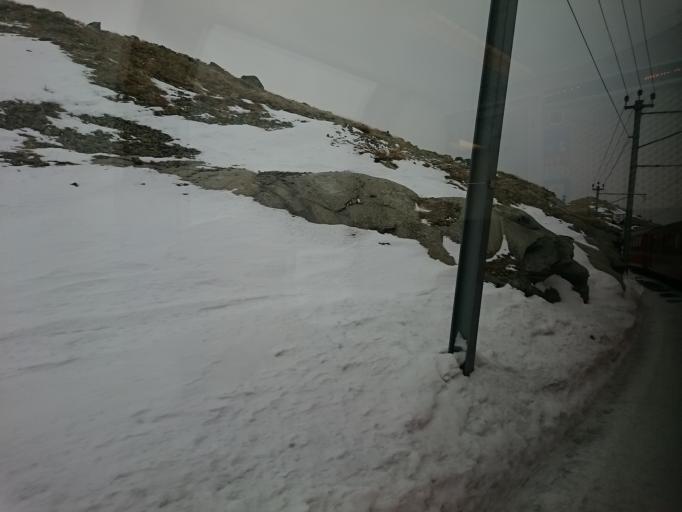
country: CH
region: Grisons
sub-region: Bernina District
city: Poschiavo
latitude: 46.3943
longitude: 10.0333
